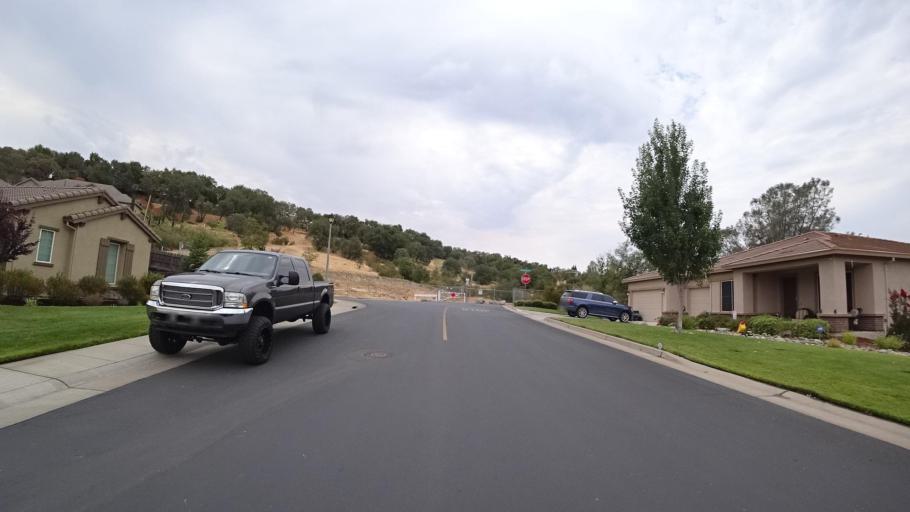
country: US
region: California
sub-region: Placer County
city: Rocklin
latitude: 38.7772
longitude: -121.2243
